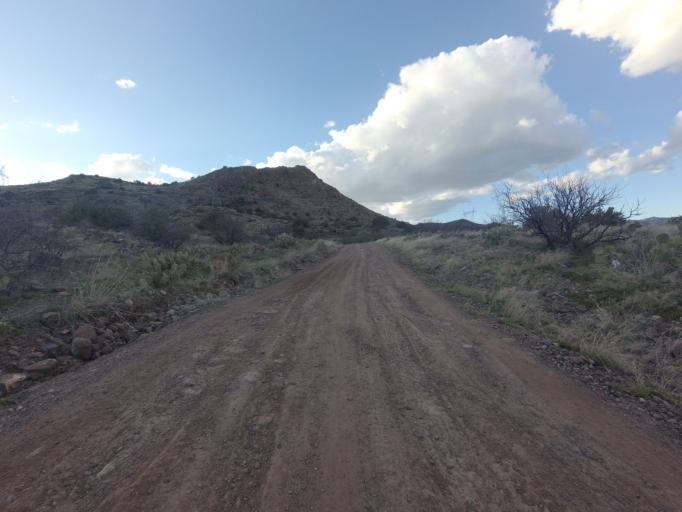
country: US
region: Arizona
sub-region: Gila County
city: Pine
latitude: 34.3659
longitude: -111.6723
